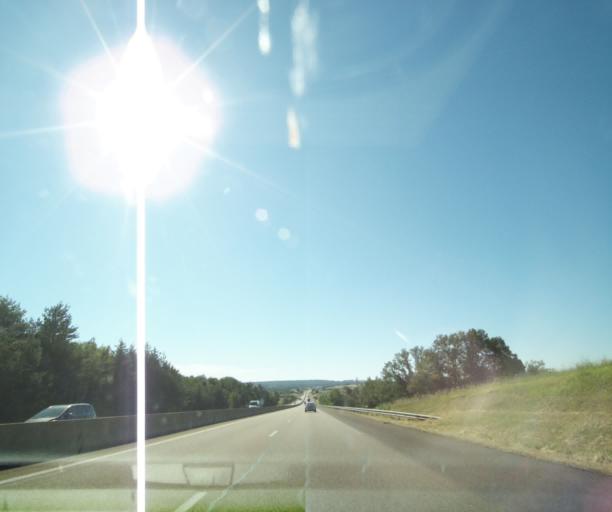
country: FR
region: Champagne-Ardenne
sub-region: Departement de la Haute-Marne
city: Rolampont
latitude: 47.9446
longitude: 5.1848
